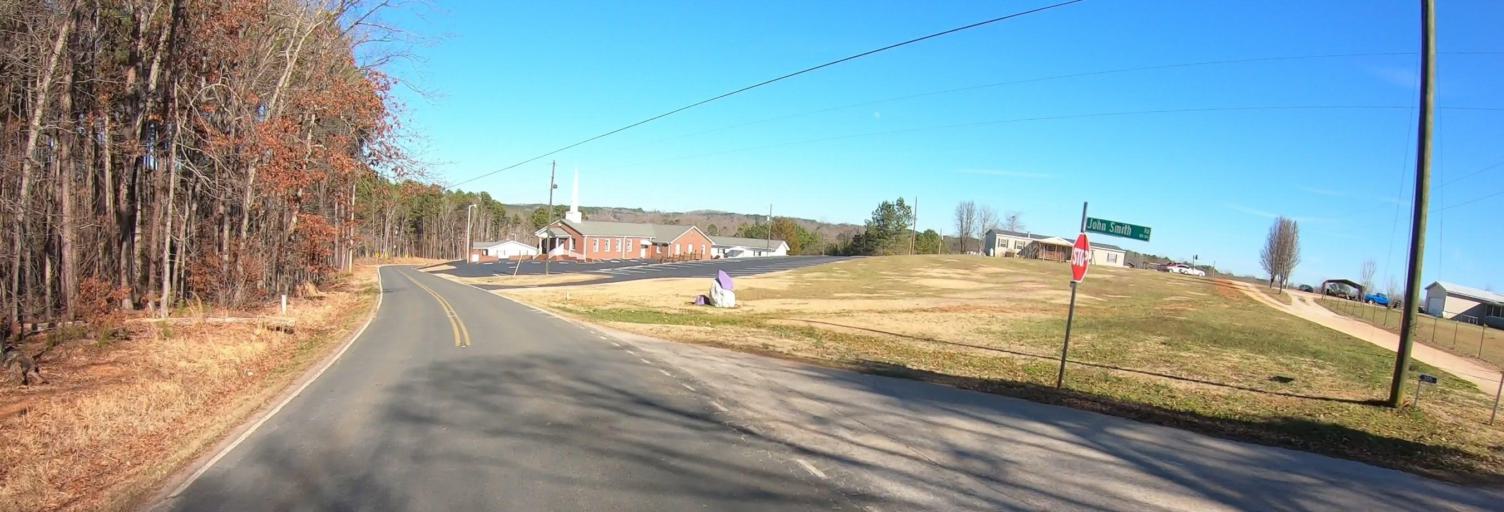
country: US
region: South Carolina
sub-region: Oconee County
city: Walhalla
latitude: 34.7191
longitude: -83.0653
